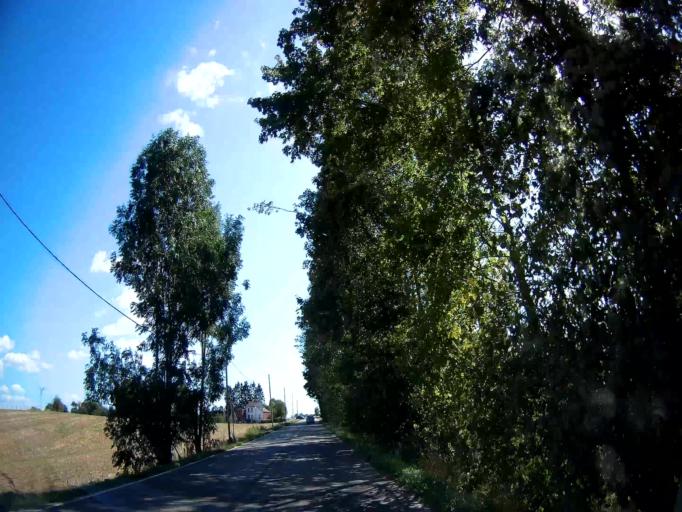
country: BE
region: Wallonia
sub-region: Province de Namur
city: Hastiere-Lavaux
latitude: 50.1871
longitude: 4.8506
